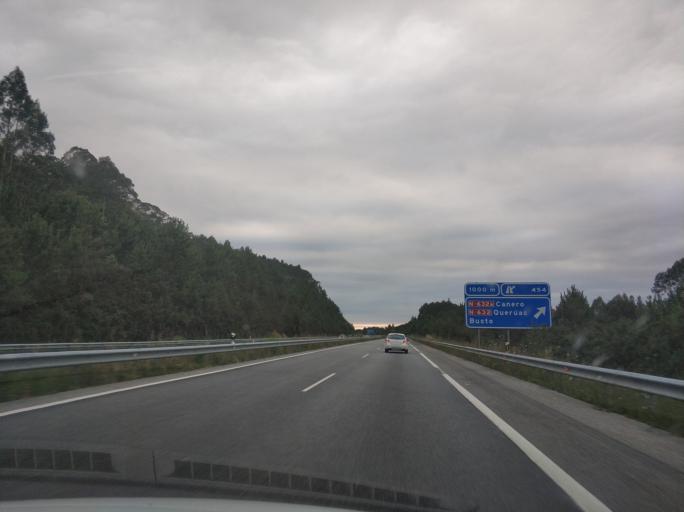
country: ES
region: Asturias
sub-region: Province of Asturias
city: Tineo
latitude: 43.5429
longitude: -6.4304
